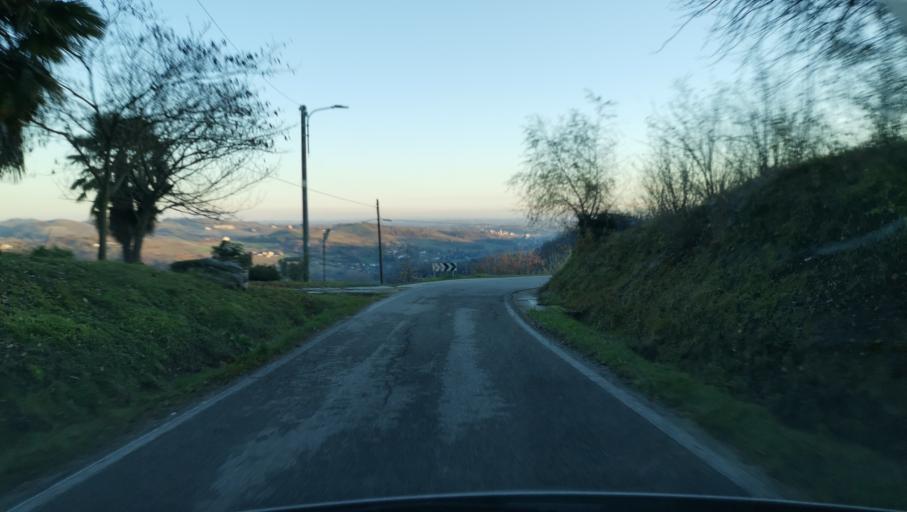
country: IT
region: Piedmont
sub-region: Provincia di Asti
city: Moncucco Torinese
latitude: 45.0757
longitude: 7.9303
